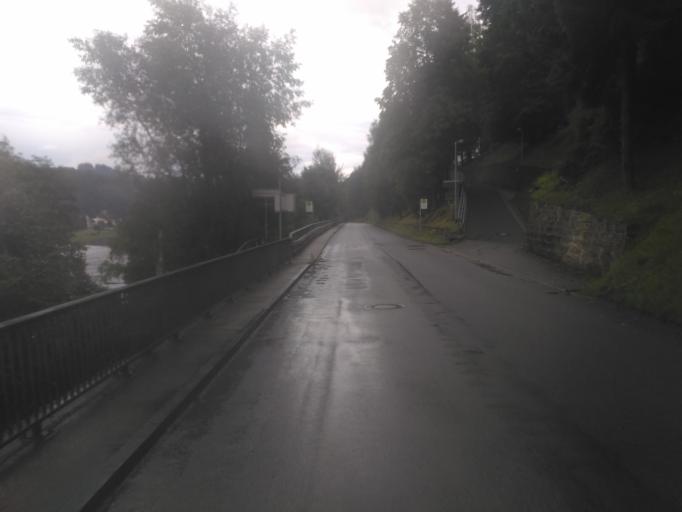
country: DE
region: Saxony
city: Bad Schandau
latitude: 50.9152
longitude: 14.1512
